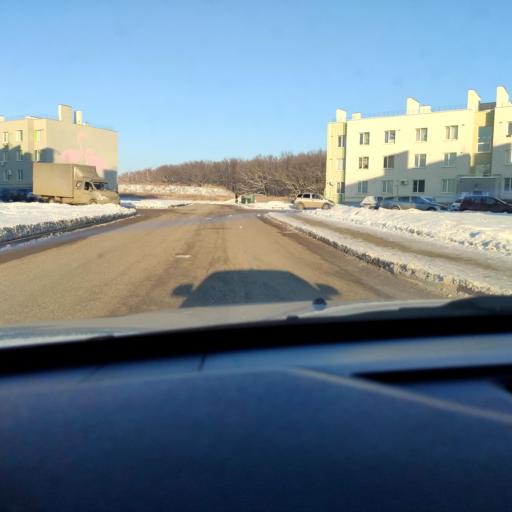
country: RU
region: Samara
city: Petra-Dubrava
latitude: 53.3052
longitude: 50.3434
